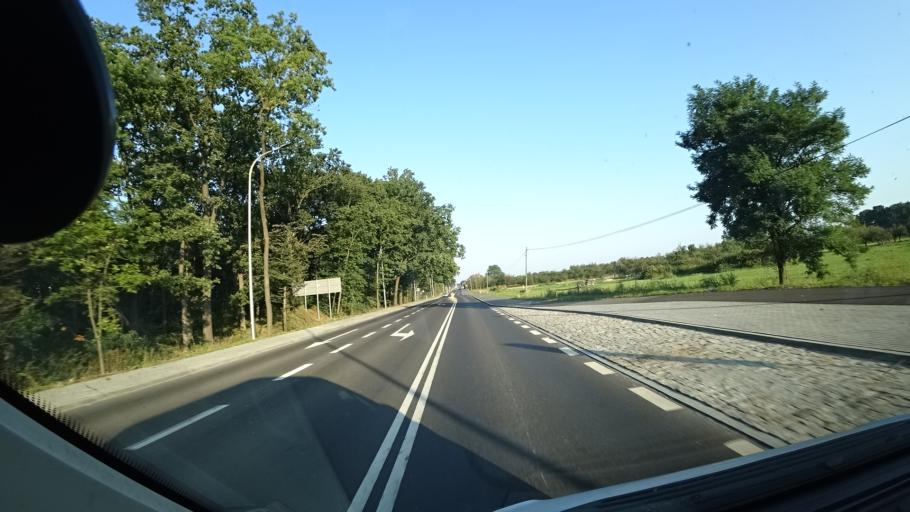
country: PL
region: Opole Voivodeship
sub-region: Powiat kedzierzynsko-kozielski
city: Bierawa
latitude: 50.2928
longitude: 18.2517
